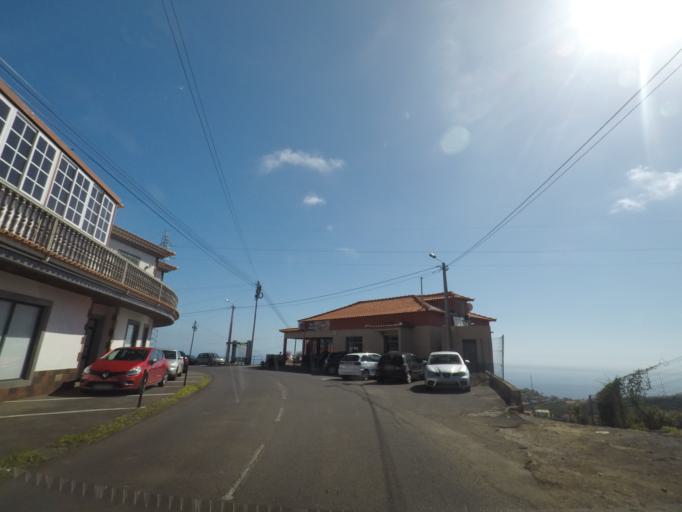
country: PT
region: Madeira
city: Ponta do Sol
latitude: 32.6961
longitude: -17.1025
